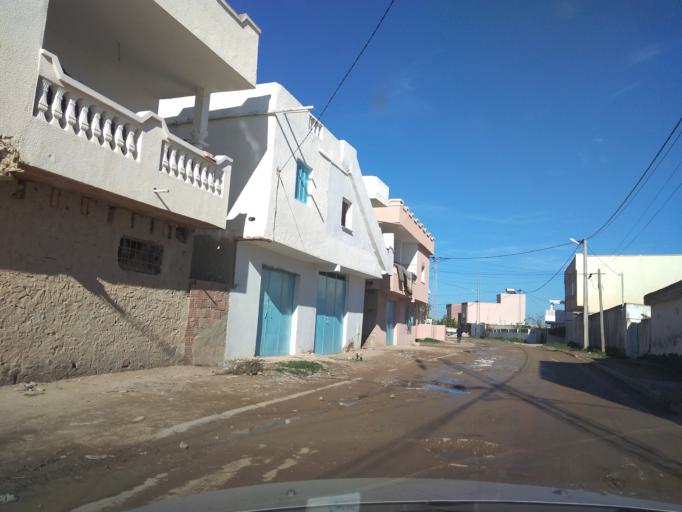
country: TN
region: Ariana
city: Qal'at al Andalus
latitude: 37.0628
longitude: 10.1245
